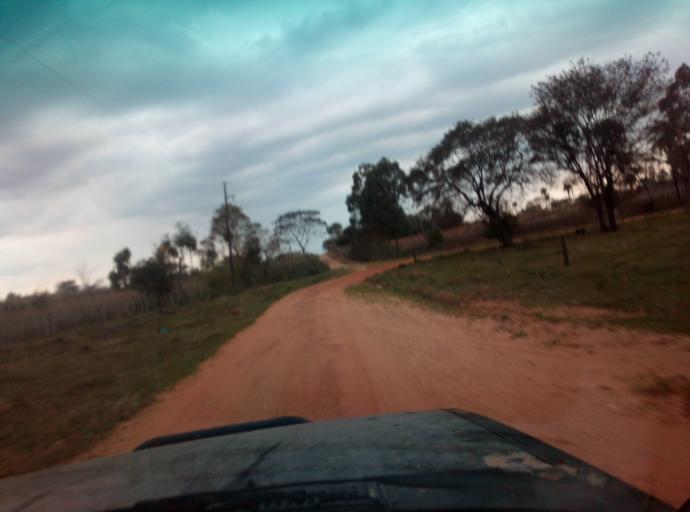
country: PY
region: Caaguazu
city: Doctor Cecilio Baez
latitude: -25.1412
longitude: -56.2239
